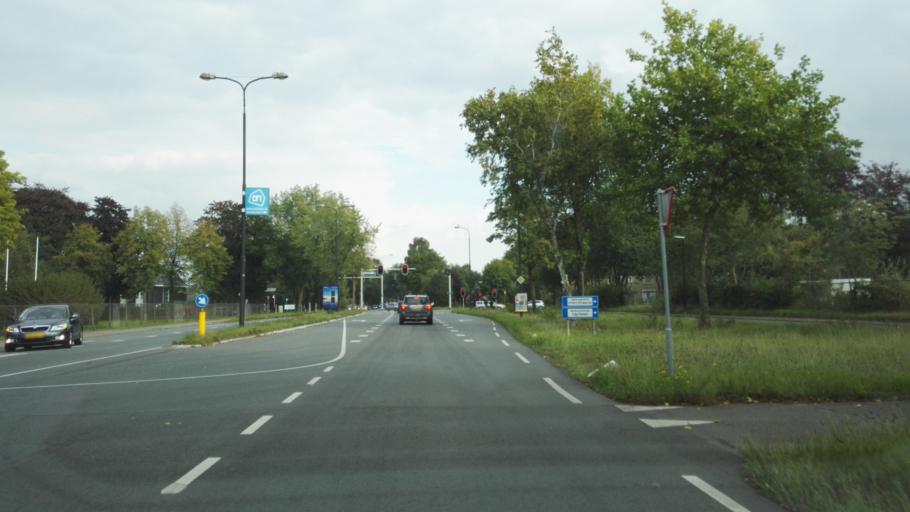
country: NL
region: Gelderland
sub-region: Gemeente Apeldoorn
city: Apeldoorn
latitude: 52.1906
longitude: 5.9427
